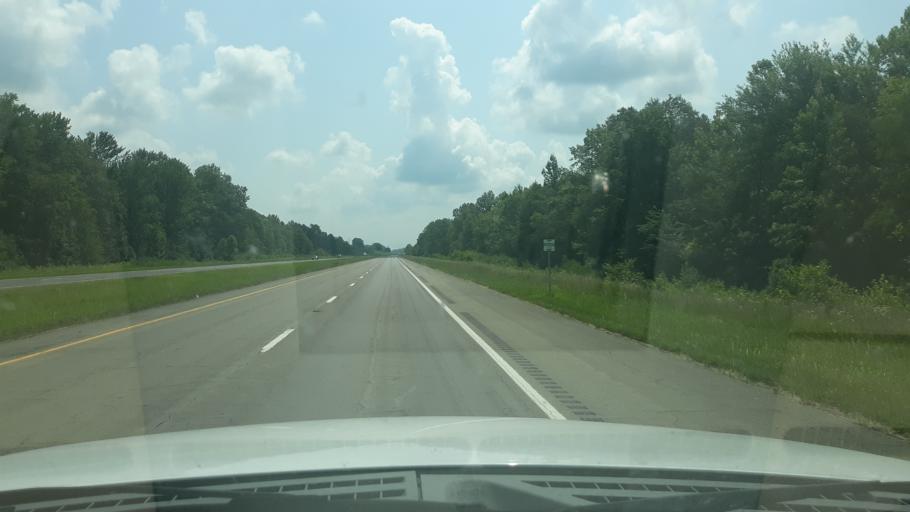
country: US
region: Illinois
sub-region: Saline County
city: Carrier Mills
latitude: 37.7342
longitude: -88.6903
